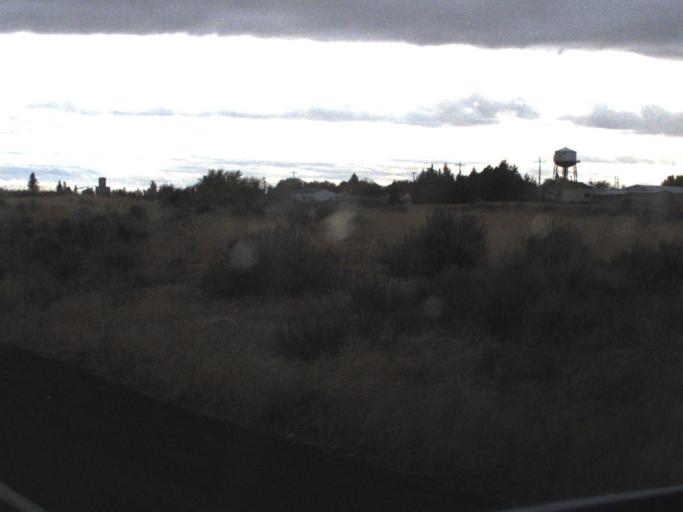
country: US
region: Washington
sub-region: Lincoln County
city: Davenport
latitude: 47.6593
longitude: -118.1410
